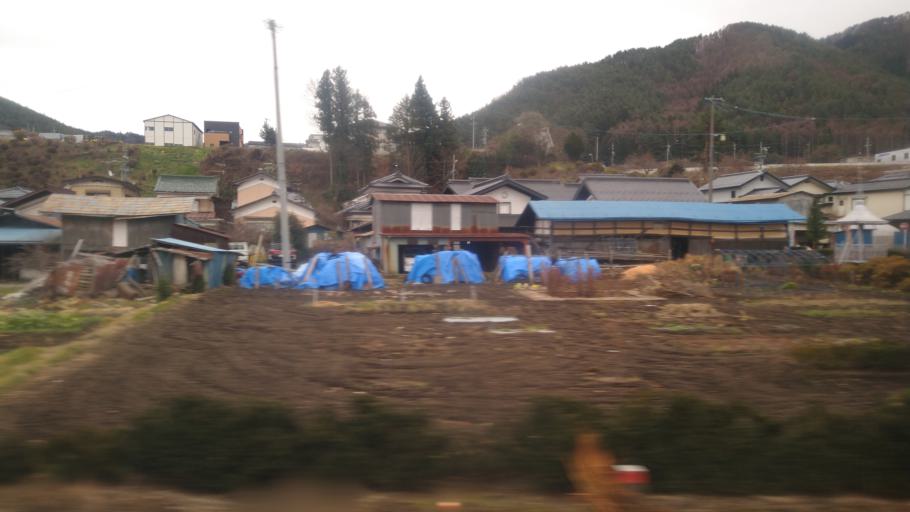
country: JP
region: Nagano
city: Shiojiri
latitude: 36.0808
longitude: 137.9108
